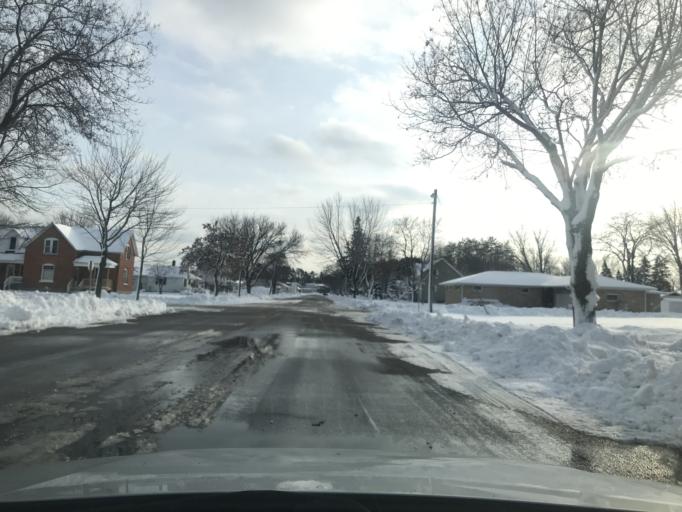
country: US
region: Wisconsin
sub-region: Marinette County
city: Peshtigo
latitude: 45.0488
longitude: -87.7548
